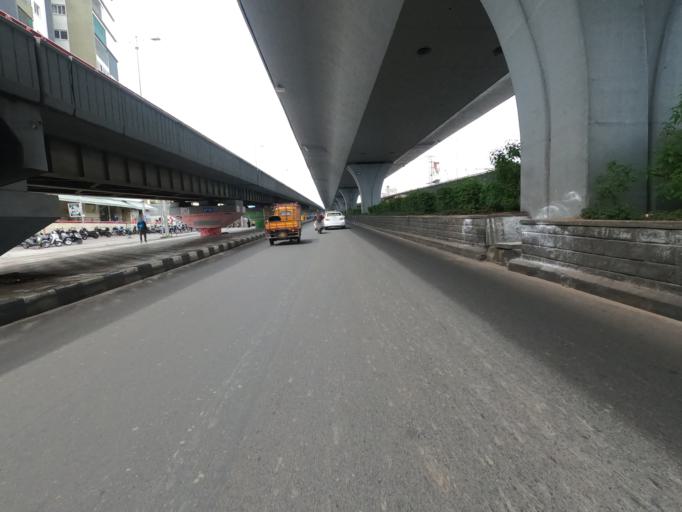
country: IN
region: Telangana
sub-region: Hyderabad
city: Hyderabad
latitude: 17.3511
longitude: 78.4176
